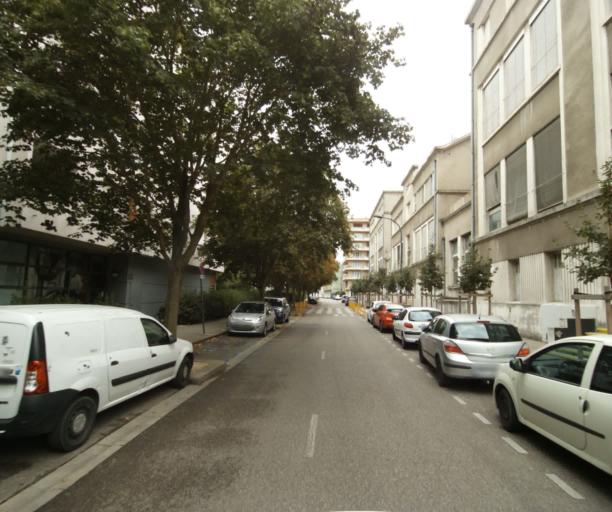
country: FR
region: Rhone-Alpes
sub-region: Departement de l'Isere
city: Grenoble
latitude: 45.1771
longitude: 5.7302
